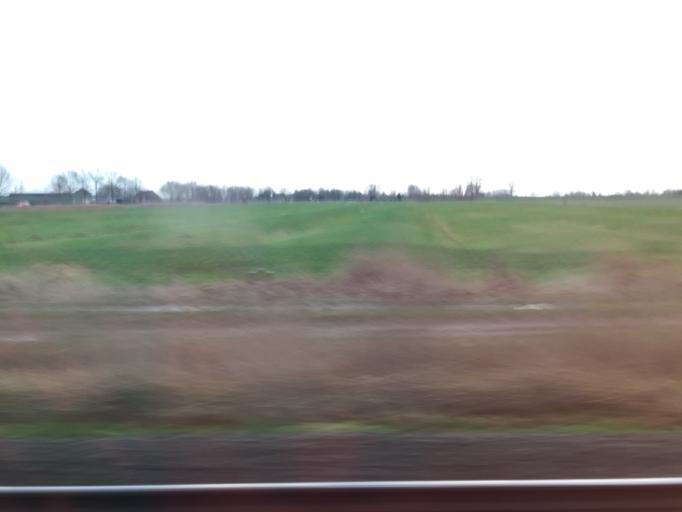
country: DE
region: Schleswig-Holstein
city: Krempdorf
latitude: 53.8149
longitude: 9.4531
